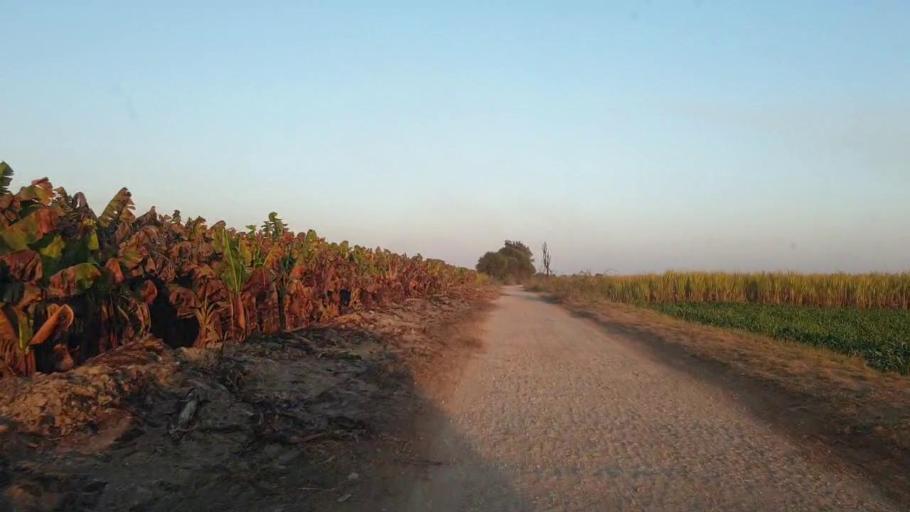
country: PK
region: Sindh
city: Tando Allahyar
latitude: 25.3634
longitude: 68.7359
